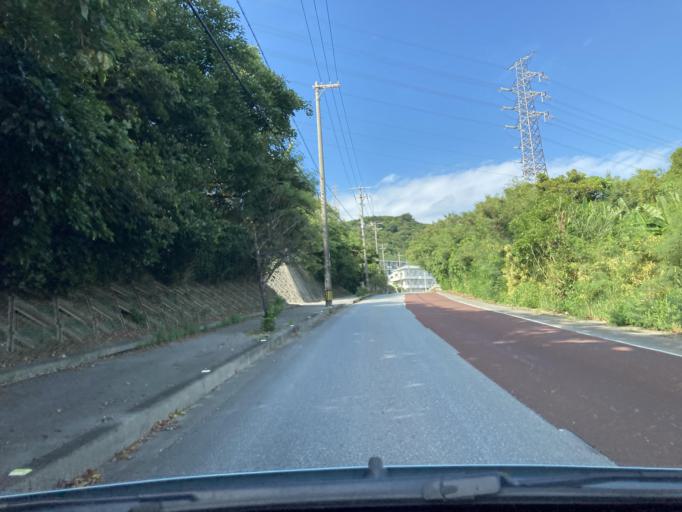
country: JP
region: Okinawa
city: Ginowan
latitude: 26.2747
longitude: 127.7968
